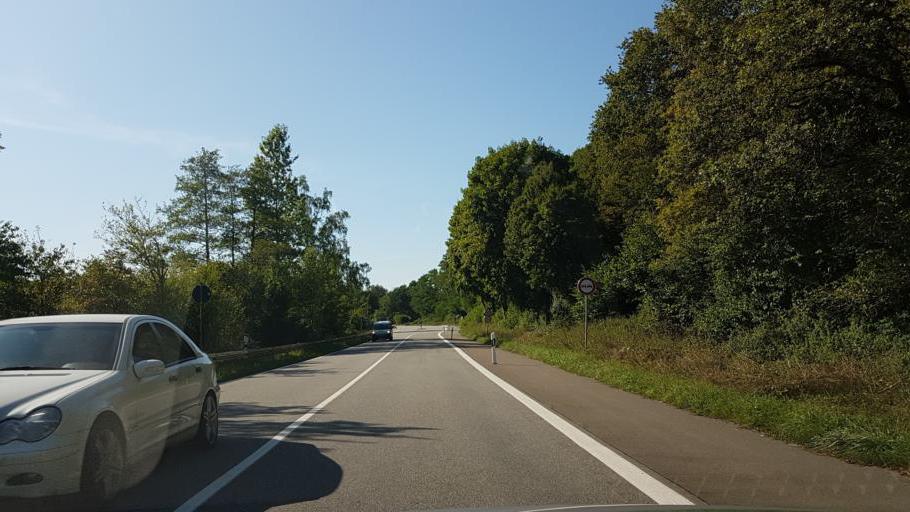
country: DE
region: Saarland
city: Schmelz
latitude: 49.4893
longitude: 6.8567
